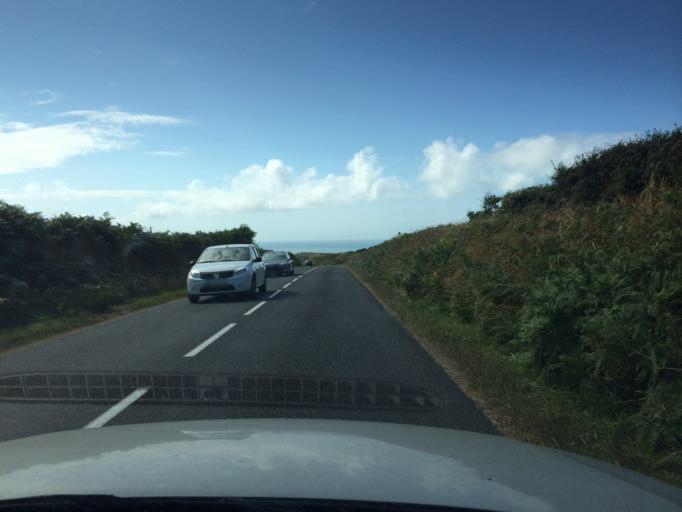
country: FR
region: Lower Normandy
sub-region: Departement de la Manche
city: Beaumont-Hague
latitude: 49.6964
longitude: -1.9219
